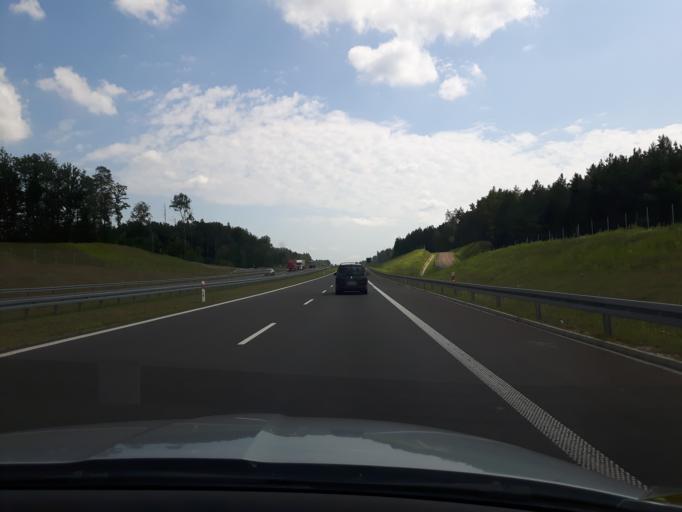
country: PL
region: Warmian-Masurian Voivodeship
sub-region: Powiat ostrodzki
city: Gierzwald
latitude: 53.5900
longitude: 20.1423
